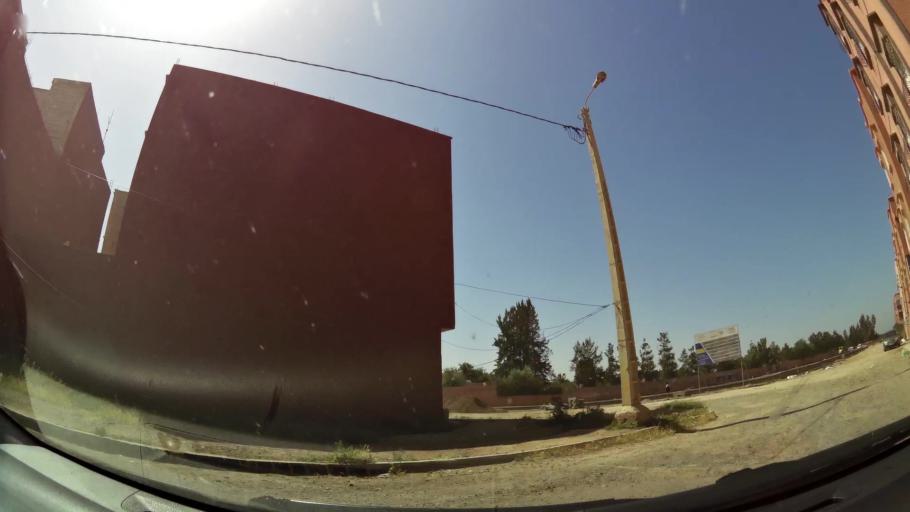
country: MA
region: Souss-Massa-Draa
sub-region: Inezgane-Ait Mellou
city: Inezgane
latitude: 30.3294
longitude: -9.5071
